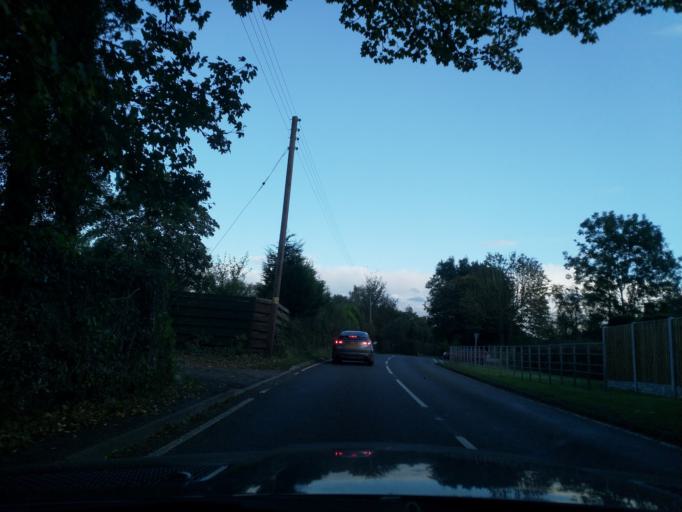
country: GB
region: England
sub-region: Solihull
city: Knowle
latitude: 52.3461
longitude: -1.7653
